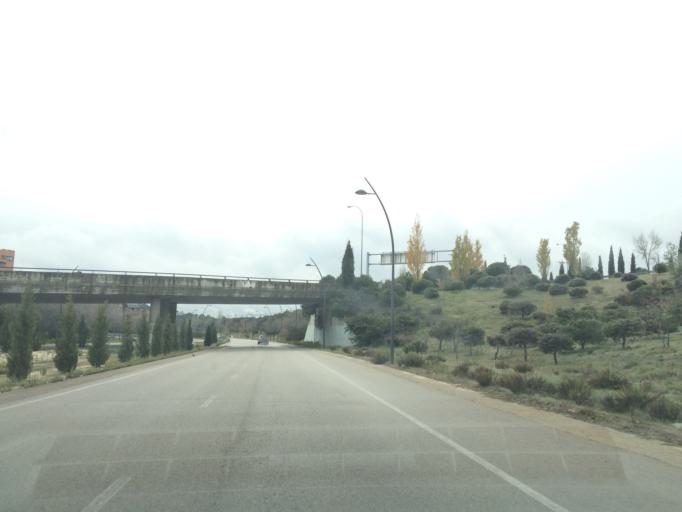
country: ES
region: Madrid
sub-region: Provincia de Madrid
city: Tres Cantos
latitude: 40.6102
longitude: -3.7190
